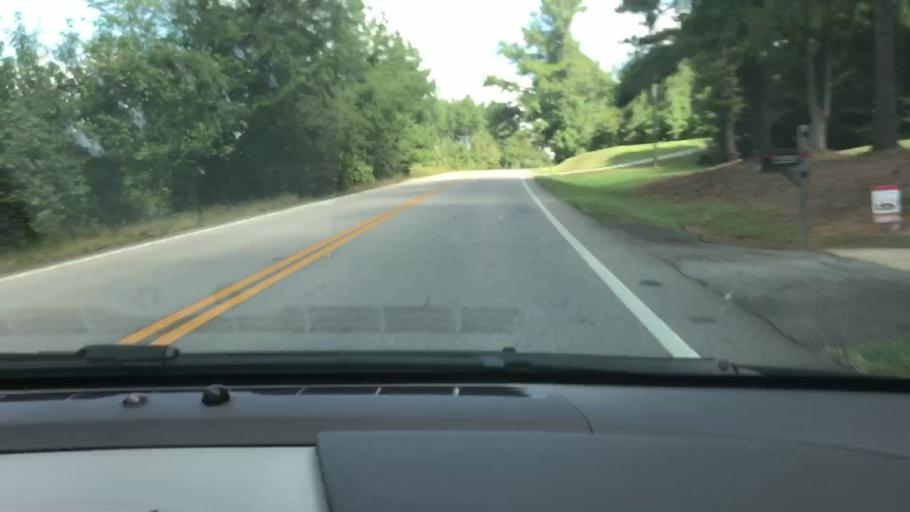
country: US
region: Georgia
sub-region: Troup County
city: La Grange
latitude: 32.9298
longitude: -85.0202
